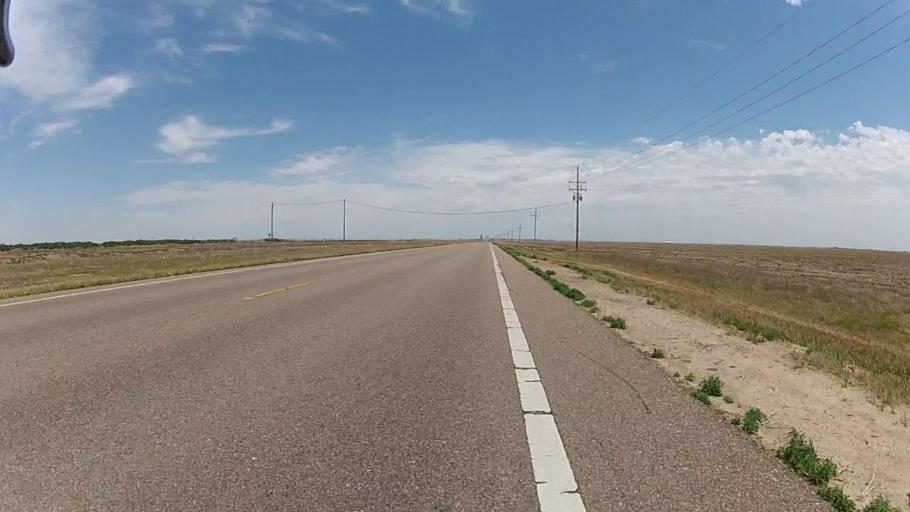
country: US
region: Kansas
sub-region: Haskell County
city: Satanta
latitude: 37.4628
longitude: -100.9176
